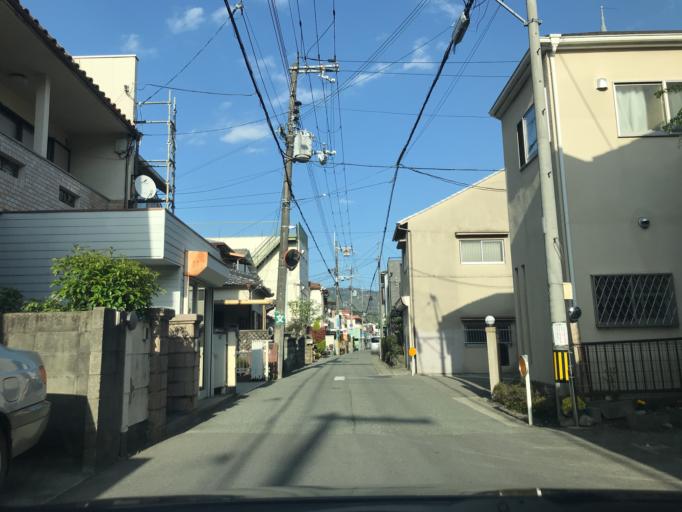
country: JP
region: Osaka
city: Ikeda
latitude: 34.8615
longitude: 135.4078
